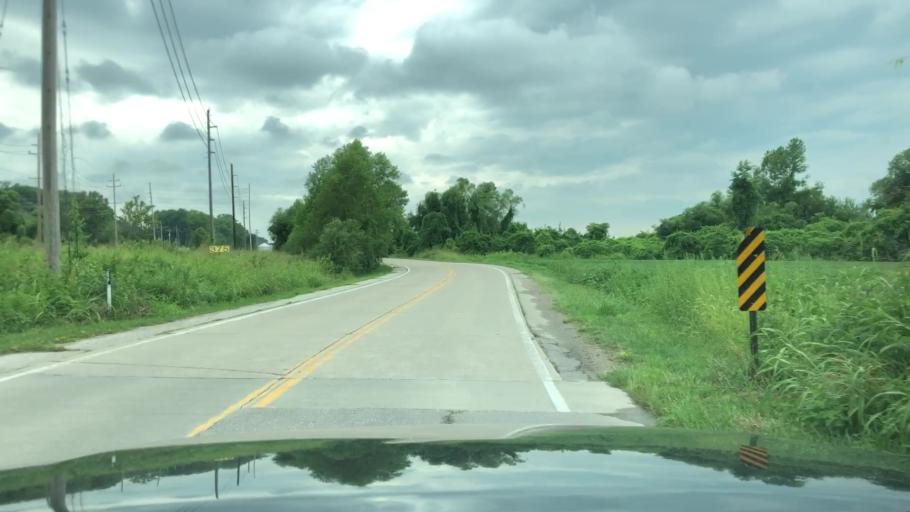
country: US
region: Missouri
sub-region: Saint Charles County
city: Saint Charles
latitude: 38.8124
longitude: -90.5378
